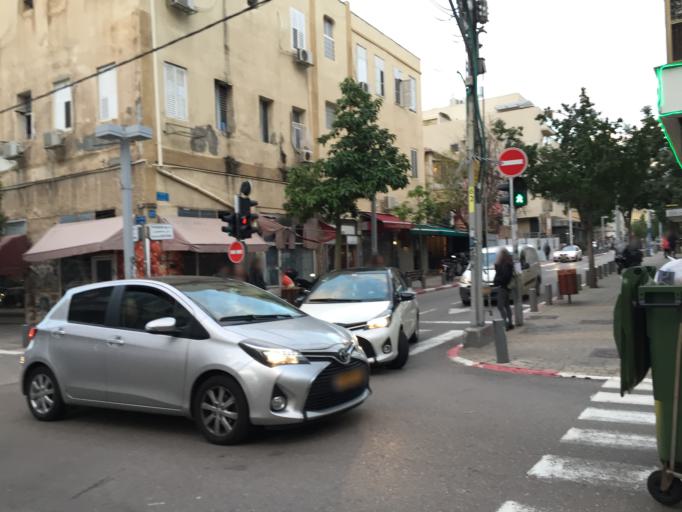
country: IL
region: Tel Aviv
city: Tel Aviv
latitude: 32.0648
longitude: 34.7710
